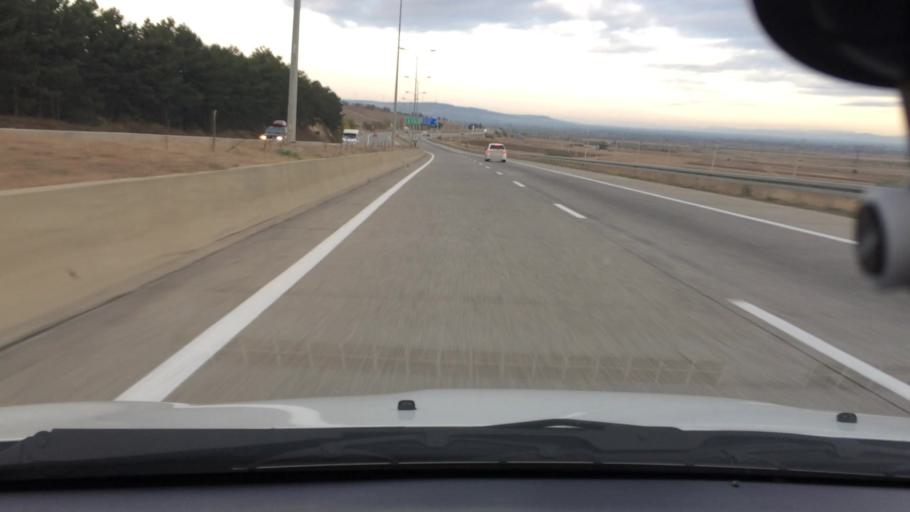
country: GE
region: Shida Kartli
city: Gori
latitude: 42.0273
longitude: 44.2051
